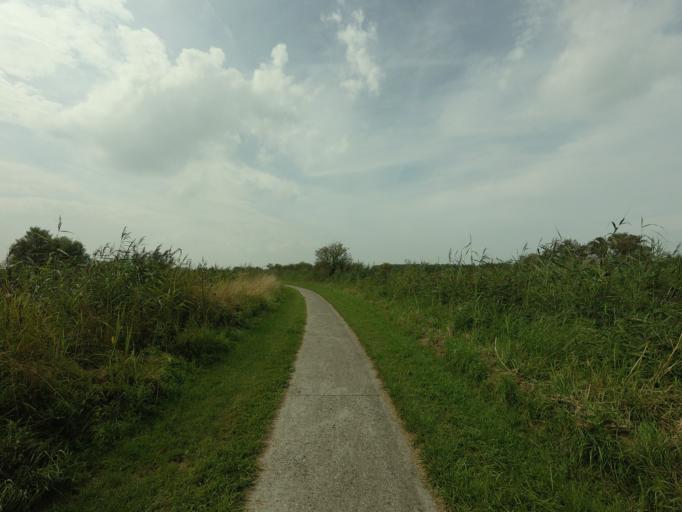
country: NL
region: Flevoland
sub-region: Gemeente Almere
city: Almere Stad
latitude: 52.4011
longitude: 5.1989
